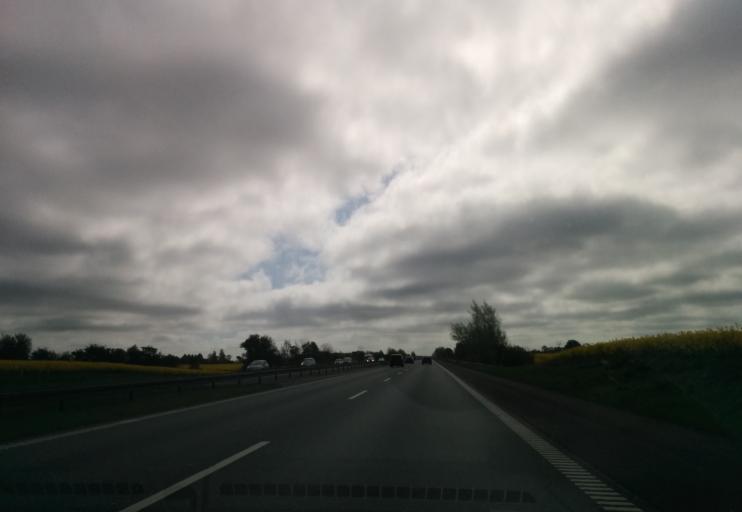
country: DK
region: South Denmark
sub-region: Assens Kommune
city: Arup
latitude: 55.4233
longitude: 10.0107
